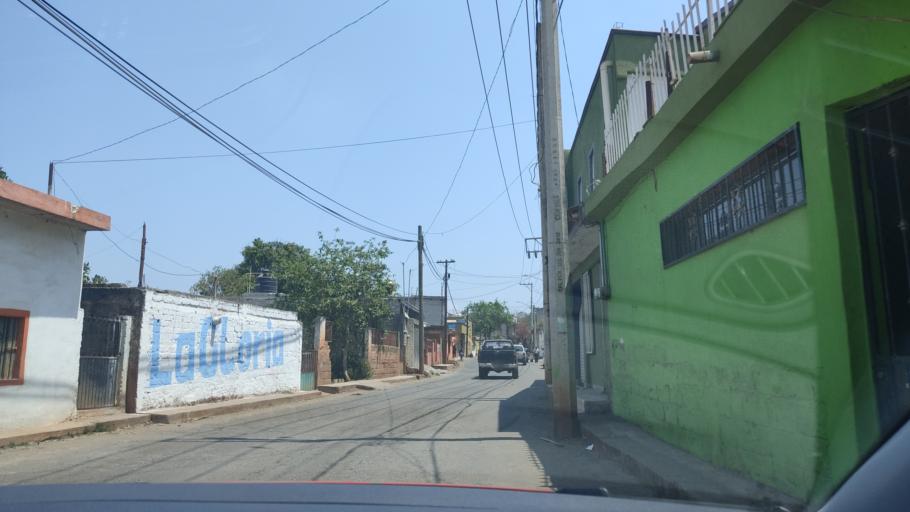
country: MX
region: Nayarit
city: Puga
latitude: 21.5838
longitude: -104.8196
